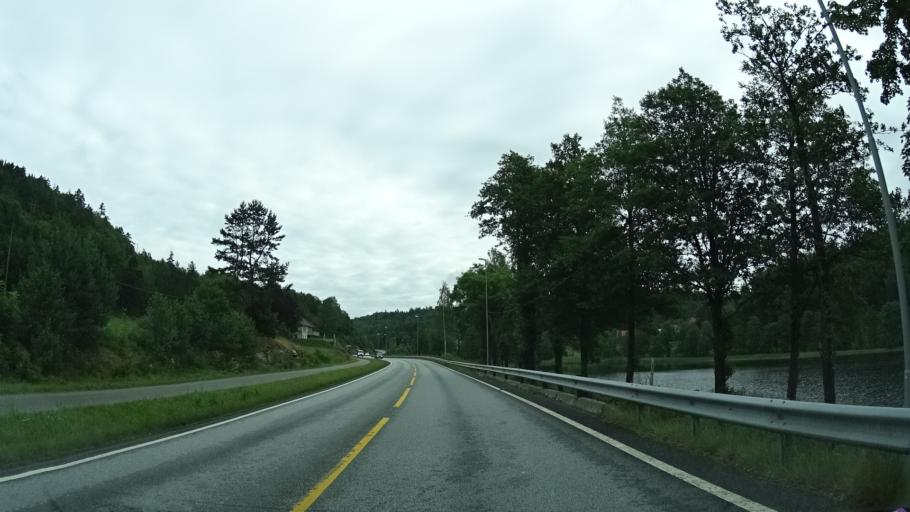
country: NO
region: Aust-Agder
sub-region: Arendal
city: Arendal
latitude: 58.5598
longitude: 8.8139
